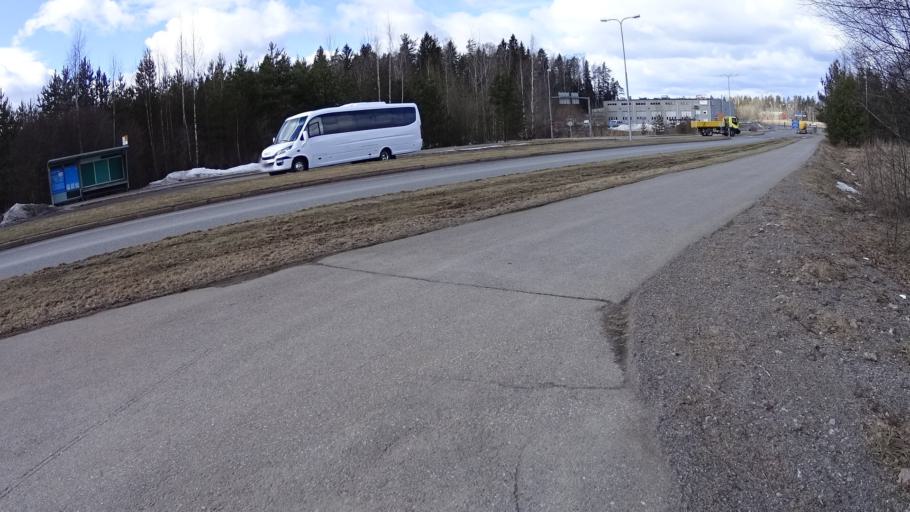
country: FI
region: Uusimaa
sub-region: Helsinki
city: Kauniainen
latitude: 60.2628
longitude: 24.7324
